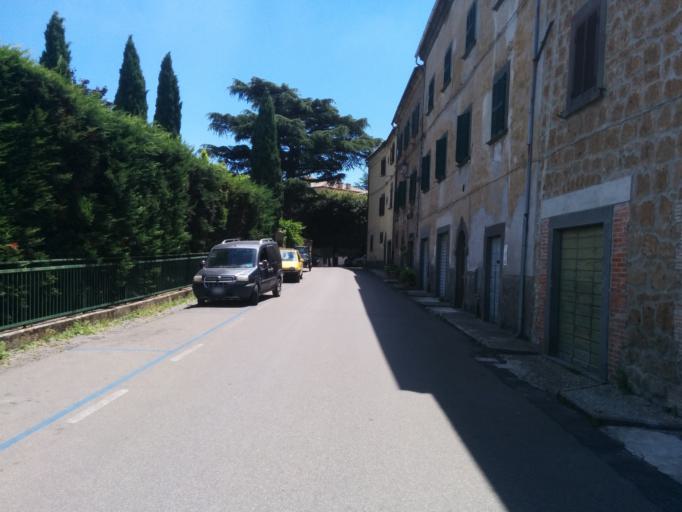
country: IT
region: Latium
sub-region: Provincia di Viterbo
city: Bagnoregio
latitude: 42.6267
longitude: 12.0980
